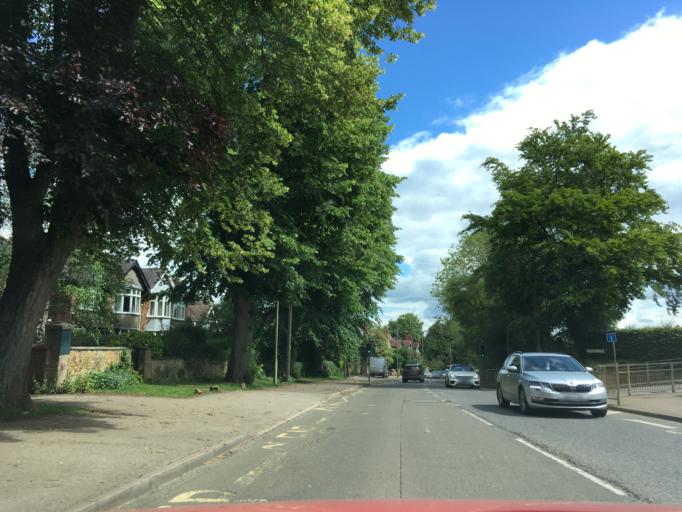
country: GB
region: England
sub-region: Oxfordshire
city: Banbury
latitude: 52.0558
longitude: -1.3431
